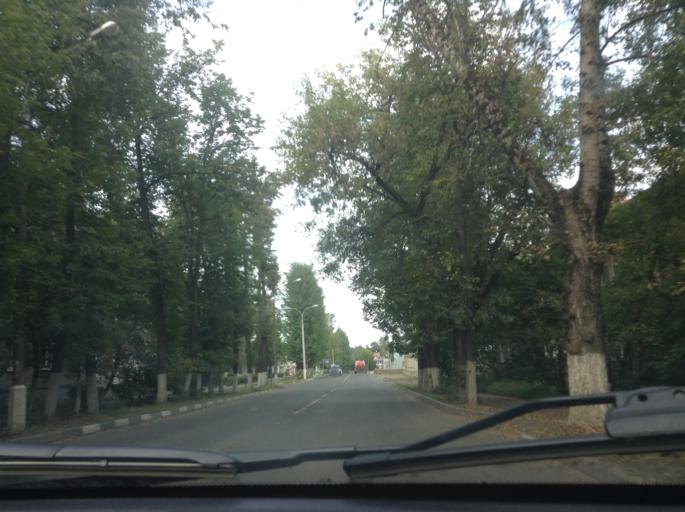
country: RU
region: Moskovskaya
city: Il'inskiy
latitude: 55.6093
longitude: 38.1085
